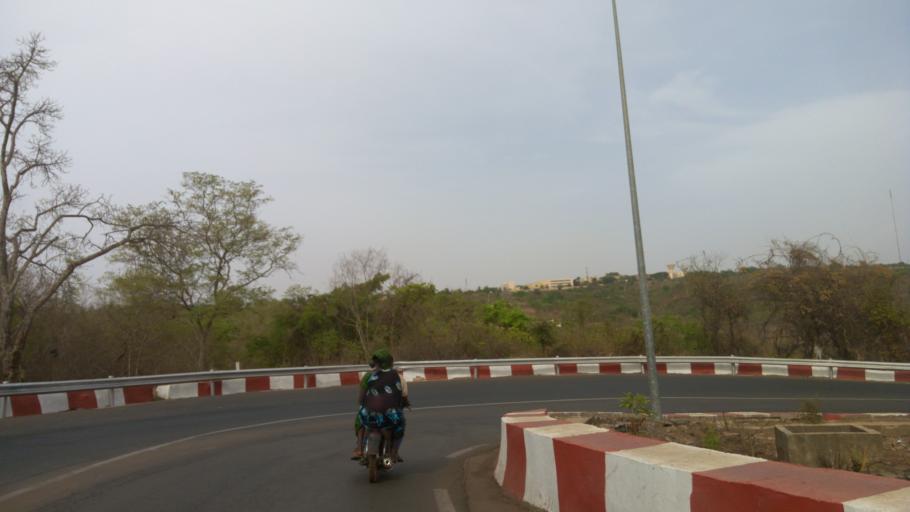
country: ML
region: Bamako
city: Bamako
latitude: 12.6712
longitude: -8.0054
